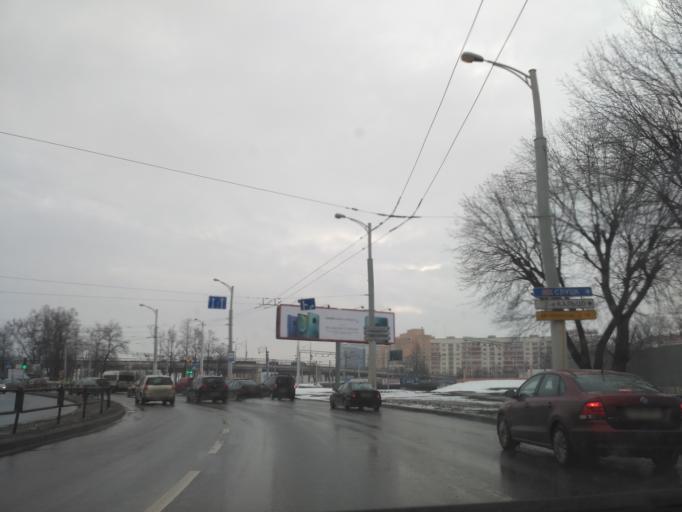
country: BY
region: Minsk
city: Minsk
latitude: 53.8938
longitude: 27.5402
